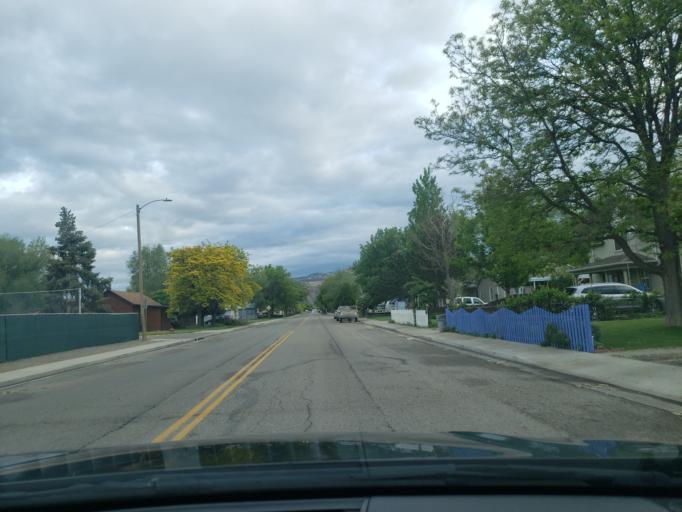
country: US
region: Colorado
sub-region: Mesa County
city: Fruita
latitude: 39.1629
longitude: -108.7314
